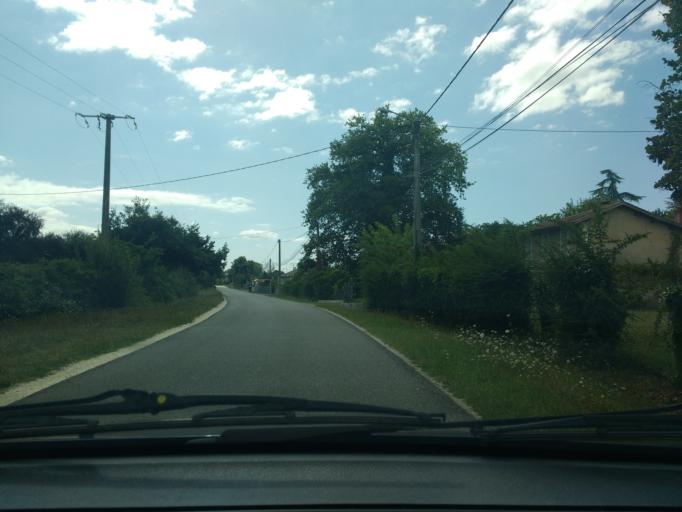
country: FR
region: Aquitaine
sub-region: Departement de la Gironde
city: Salles
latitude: 44.5638
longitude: -0.8448
